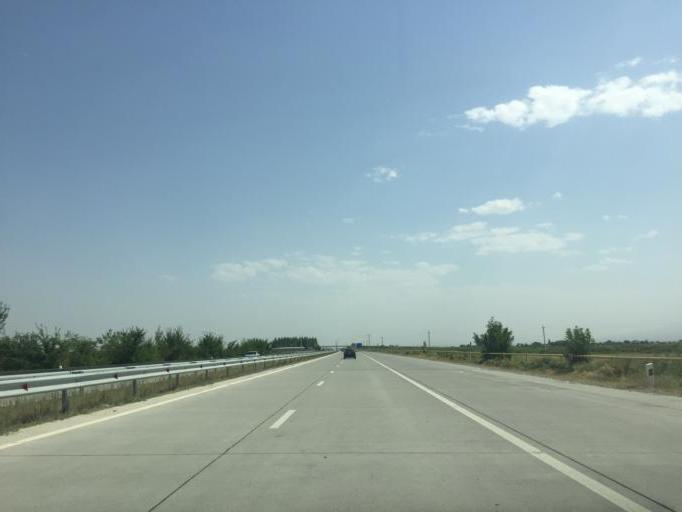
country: AM
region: Ararat
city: Mrgavet
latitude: 40.0132
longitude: 44.4694
